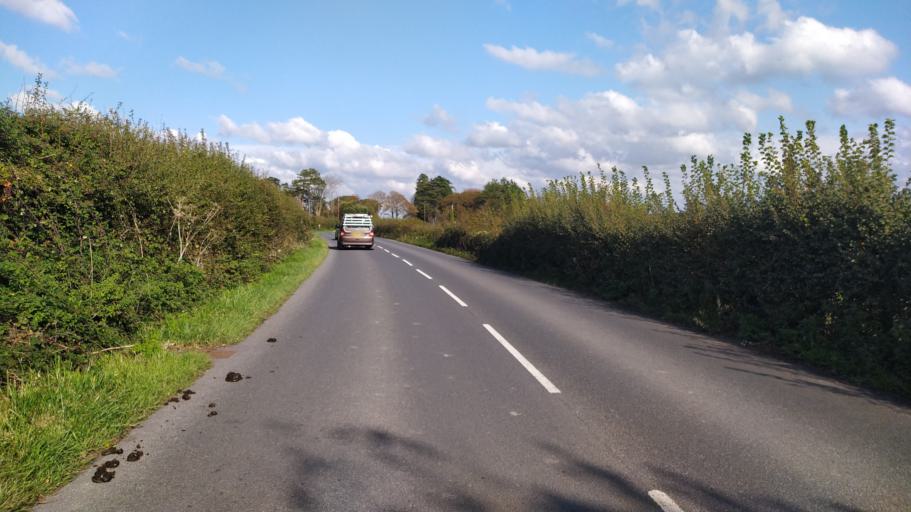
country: GB
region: England
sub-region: Isle of Wight
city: Freshwater
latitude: 50.6930
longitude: -1.5231
